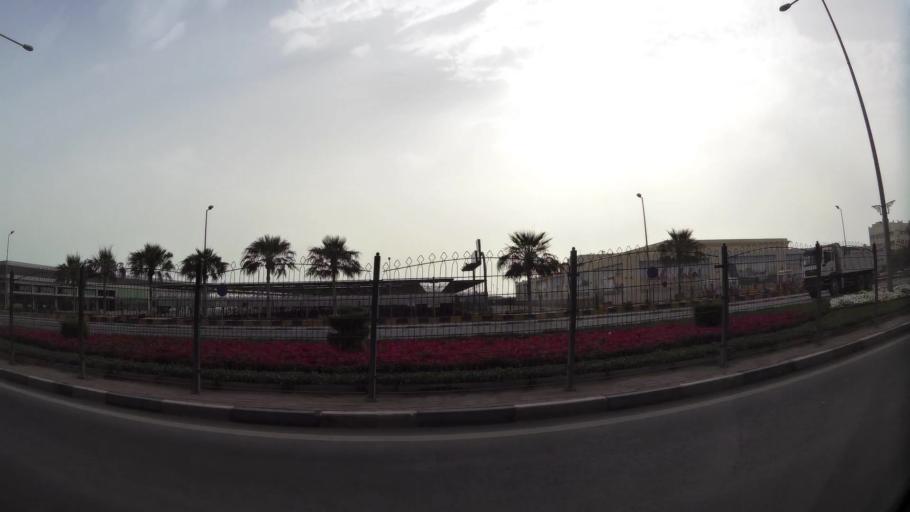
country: QA
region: Baladiyat ad Dawhah
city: Doha
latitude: 25.2788
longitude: 51.5521
